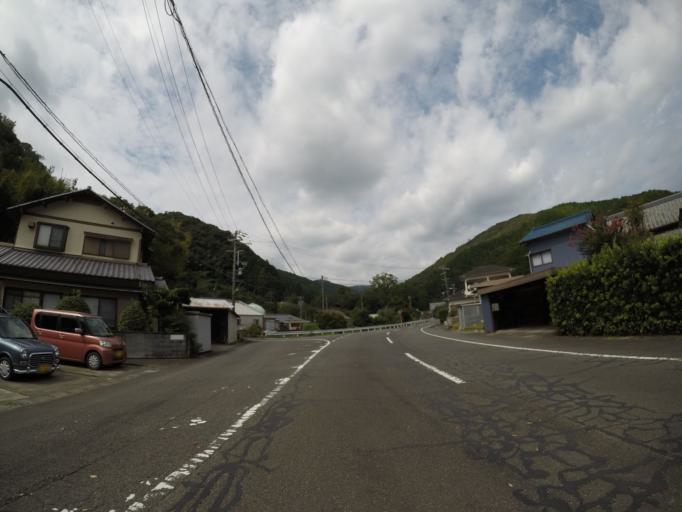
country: JP
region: Shizuoka
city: Shimada
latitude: 34.8714
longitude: 138.1809
